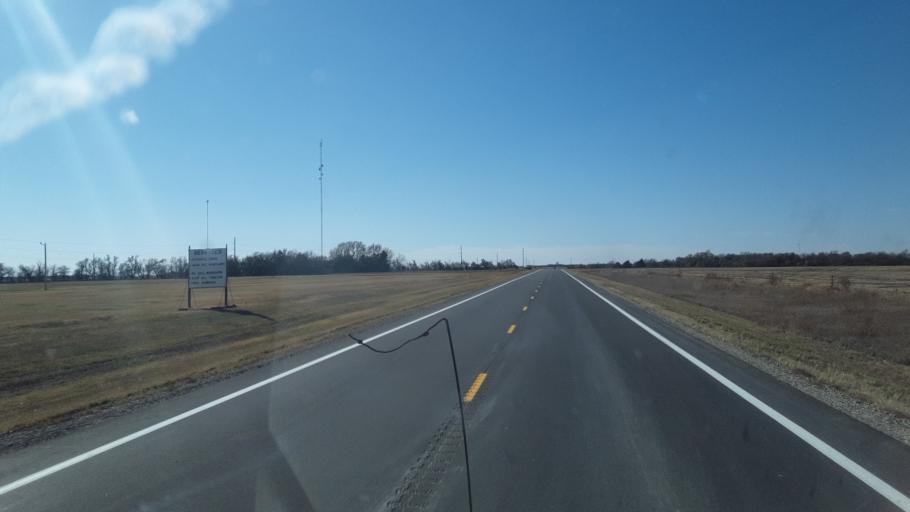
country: US
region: Kansas
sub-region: Rice County
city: Lyons
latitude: 38.3718
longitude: -98.1387
